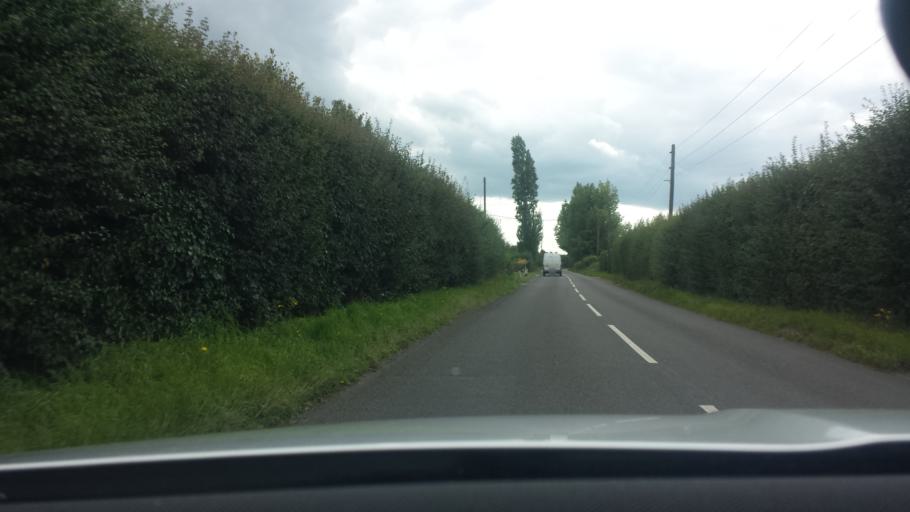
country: GB
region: England
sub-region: Kent
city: Marden
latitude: 51.1856
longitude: 0.4928
